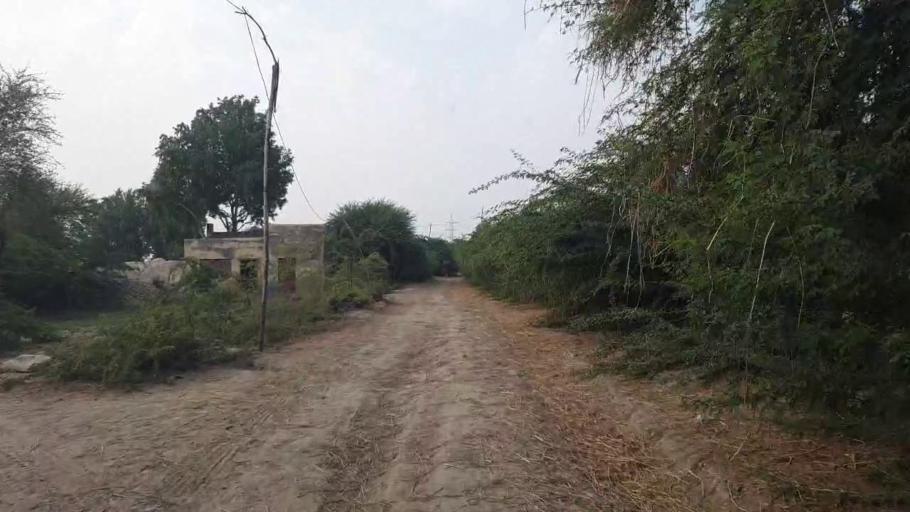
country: PK
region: Sindh
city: Talhar
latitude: 24.8454
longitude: 68.8126
